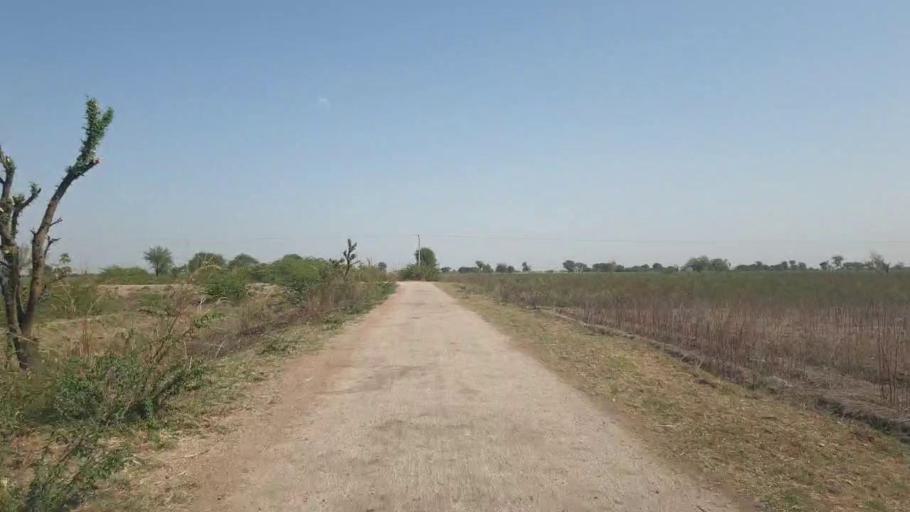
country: PK
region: Sindh
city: Umarkot
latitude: 25.3022
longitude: 69.6180
